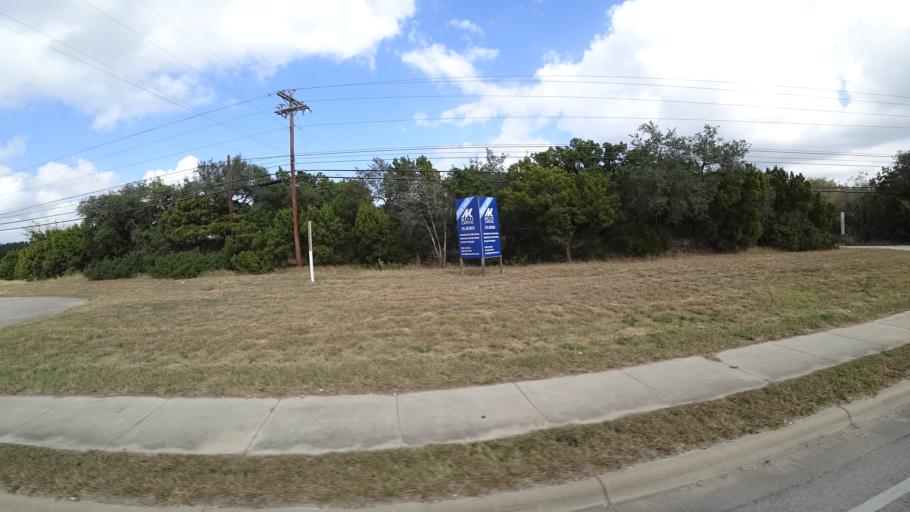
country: US
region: Texas
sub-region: Williamson County
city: Anderson Mill
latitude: 30.4597
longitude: -97.8373
